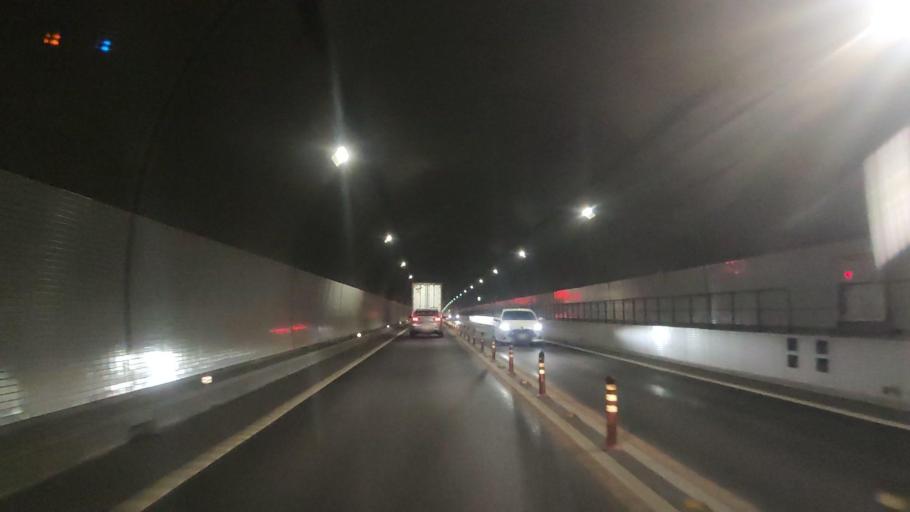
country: JP
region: Fukuoka
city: Kanda
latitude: 33.7615
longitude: 130.9613
